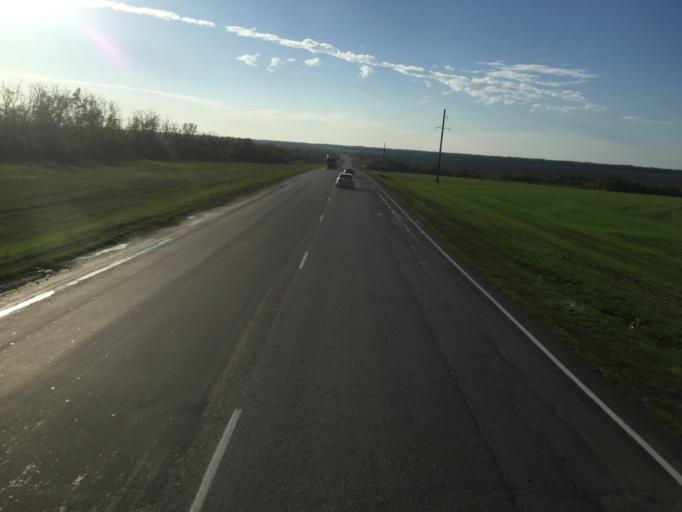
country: RU
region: Rostov
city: Mechetinskaya
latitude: 46.7784
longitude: 40.4160
